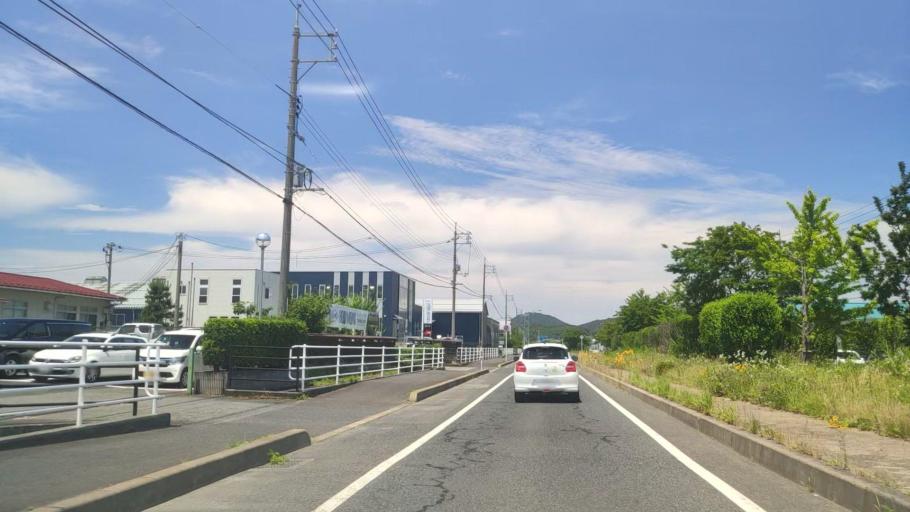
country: JP
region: Tottori
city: Tottori
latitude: 35.4586
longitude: 134.2430
